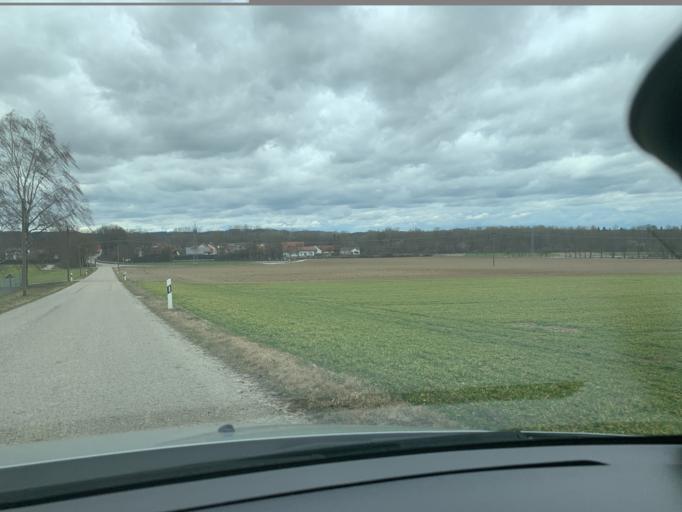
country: DE
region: Bavaria
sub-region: Lower Bavaria
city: Eching
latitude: 48.5056
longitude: 12.0816
